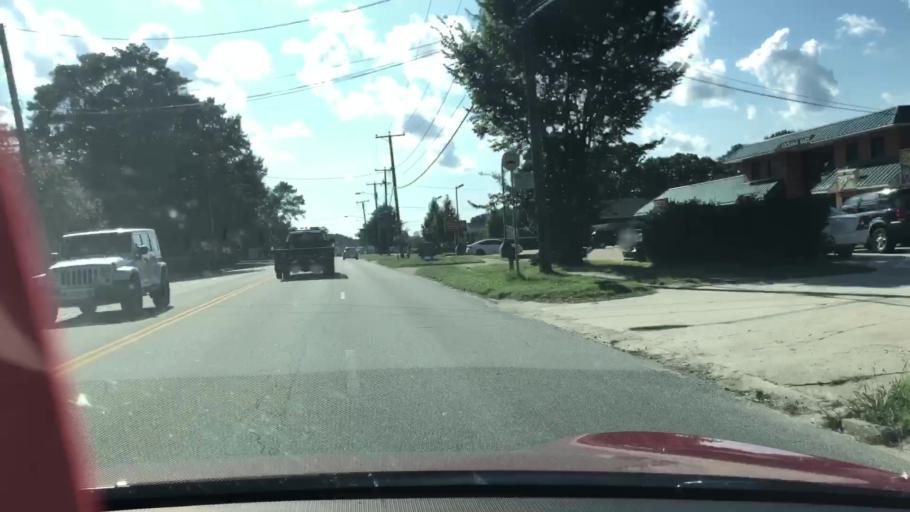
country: US
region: Virginia
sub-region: City of Virginia Beach
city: Virginia Beach
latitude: 36.8424
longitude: -76.0178
